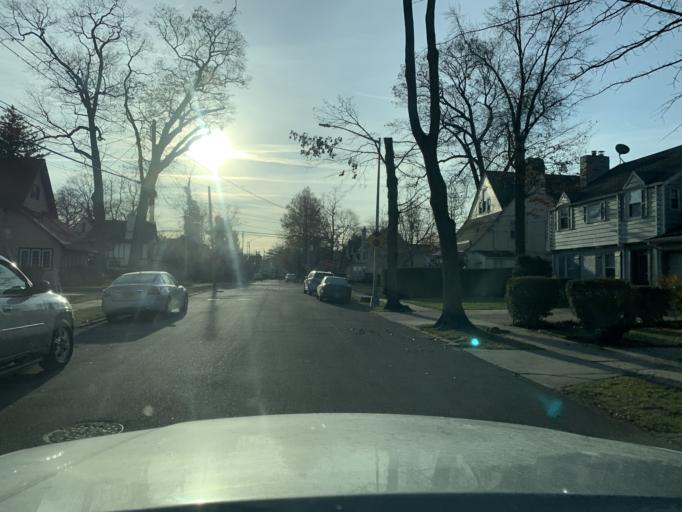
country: US
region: New York
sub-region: Queens County
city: Jamaica
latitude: 40.6945
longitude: -73.7746
